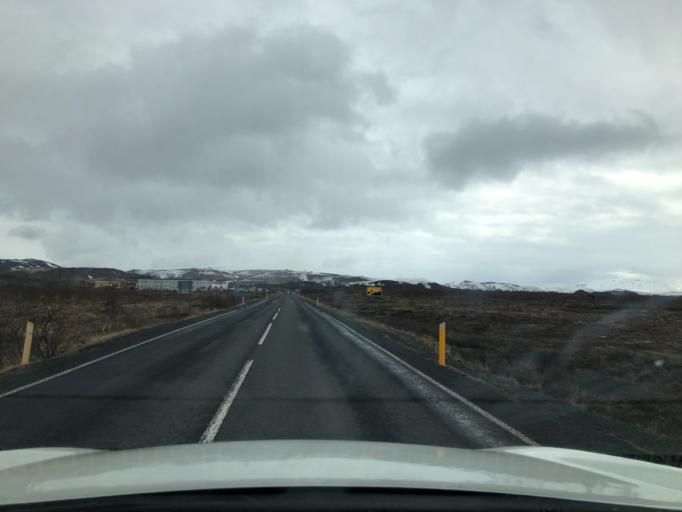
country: IS
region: Northeast
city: Laugar
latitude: 65.6395
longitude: -16.9047
